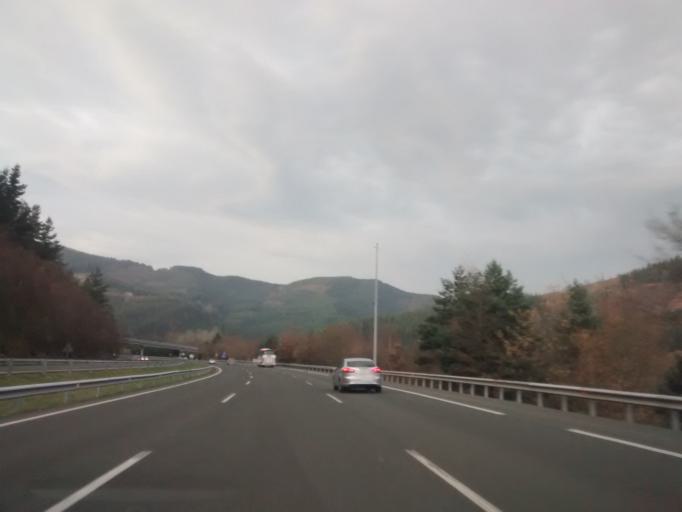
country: ES
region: Basque Country
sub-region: Provincia de Alava
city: Lezama
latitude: 43.0490
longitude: -2.9244
